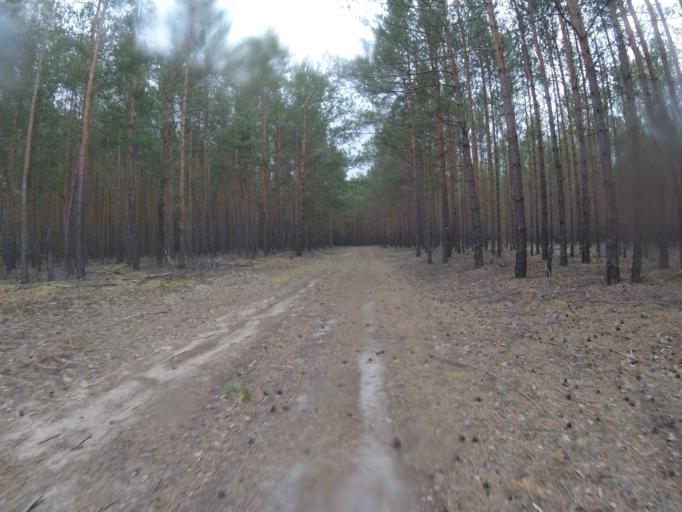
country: DE
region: Brandenburg
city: Gross Koris
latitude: 52.1916
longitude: 13.6560
